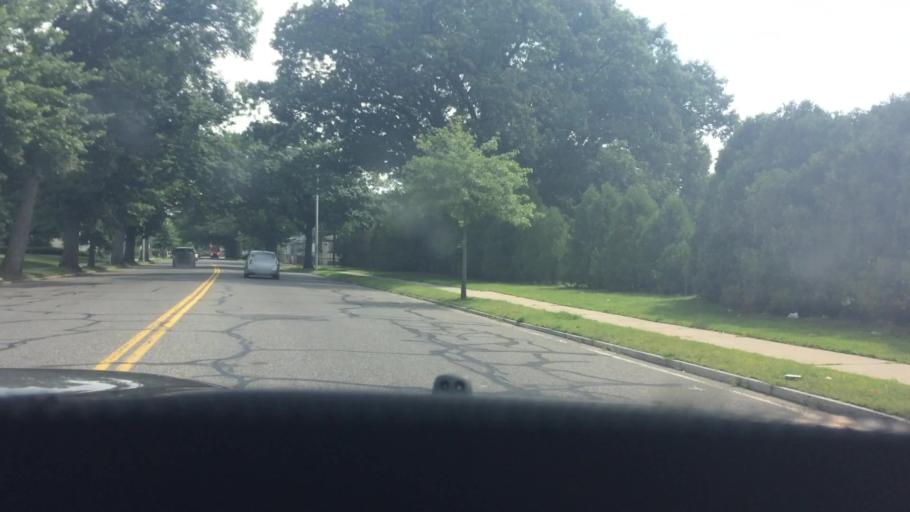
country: US
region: Massachusetts
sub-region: Hampden County
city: Springfield
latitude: 42.1204
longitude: -72.5918
